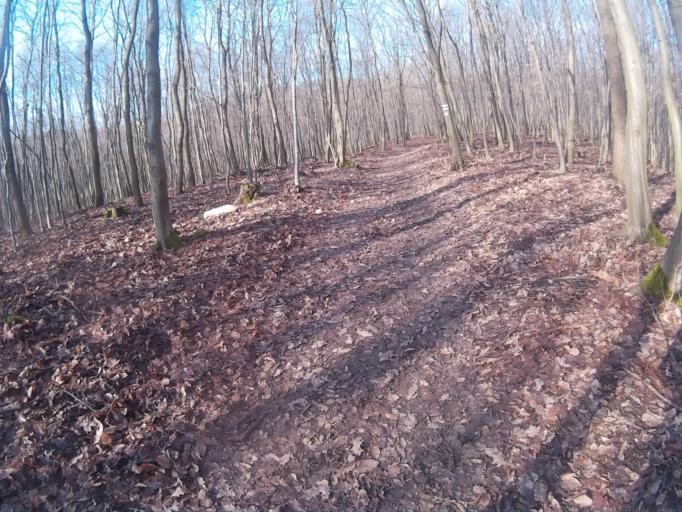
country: HU
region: Komarom-Esztergom
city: Tarjan
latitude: 47.6534
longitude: 18.4921
